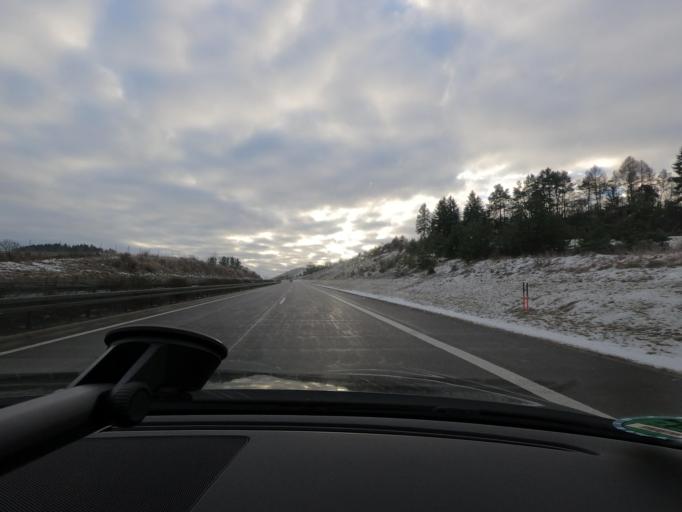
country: DE
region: Thuringia
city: Veilsdorf
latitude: 50.4708
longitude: 10.8287
